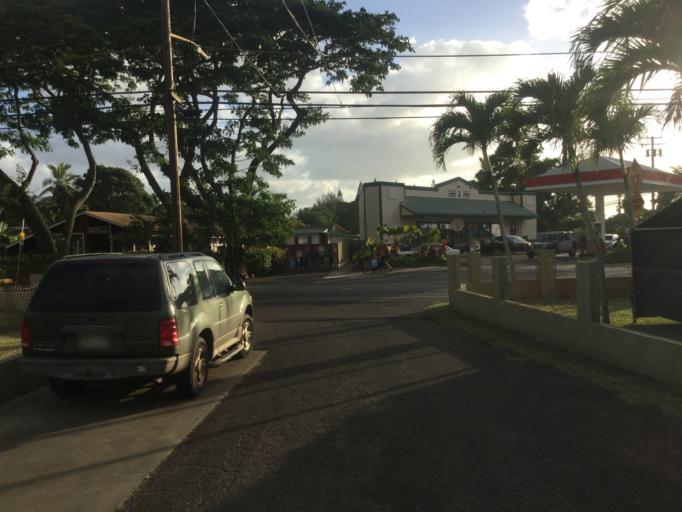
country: US
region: Hawaii
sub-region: Honolulu County
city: Hale'iwa
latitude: 21.5925
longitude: -158.1030
